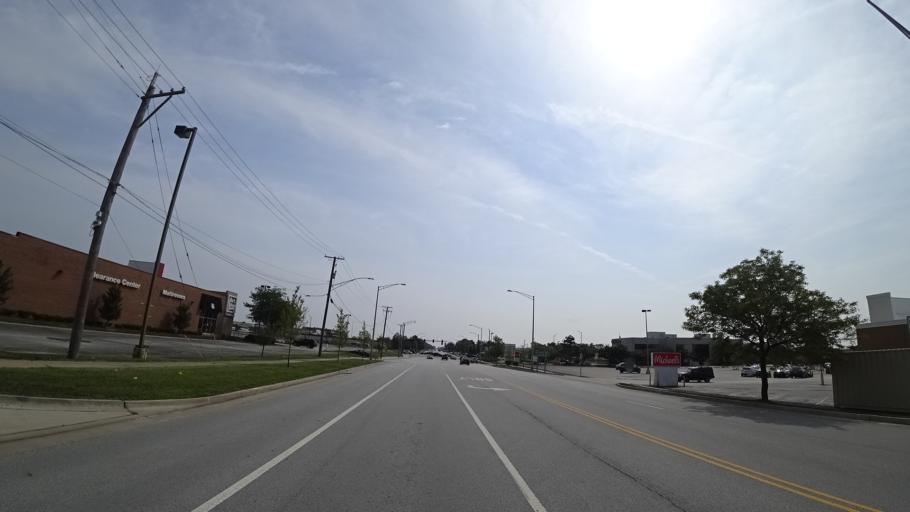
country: US
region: Illinois
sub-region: Cook County
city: Orland Park
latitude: 41.6159
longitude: -87.8556
